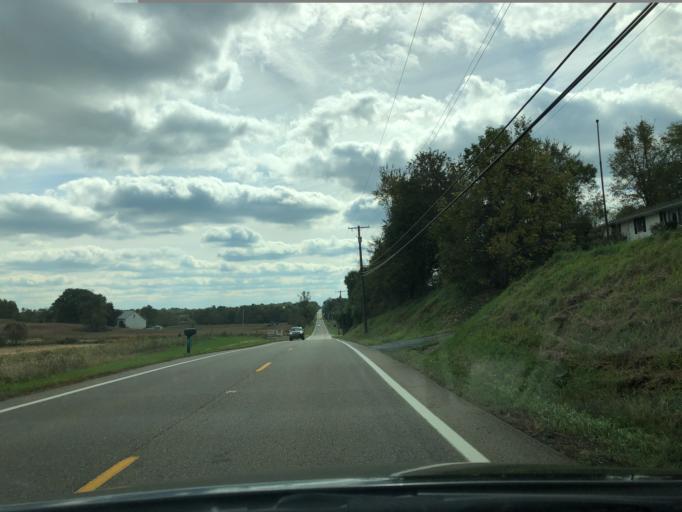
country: US
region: Ohio
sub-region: Stark County
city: Brewster
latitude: 40.7375
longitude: -81.5961
